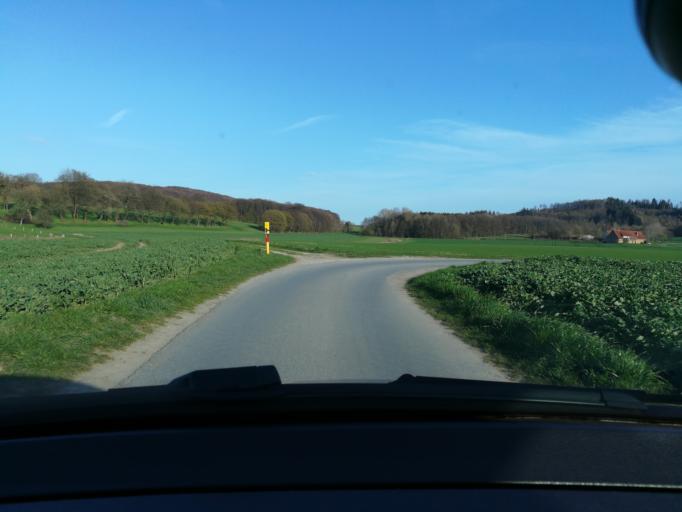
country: DE
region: North Rhine-Westphalia
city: Borgholzhausen
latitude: 52.0944
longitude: 8.3035
